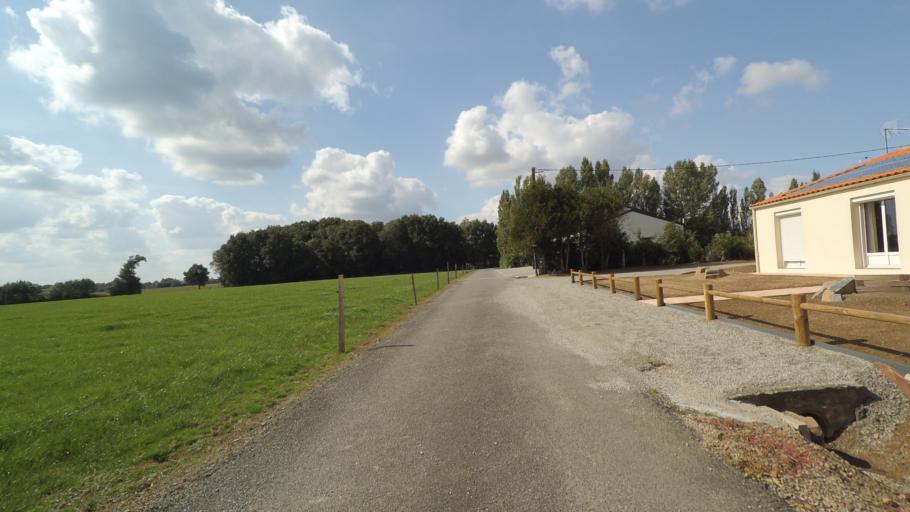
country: FR
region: Pays de la Loire
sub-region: Departement de la Vendee
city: Bouffere
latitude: 46.9632
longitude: -1.3722
